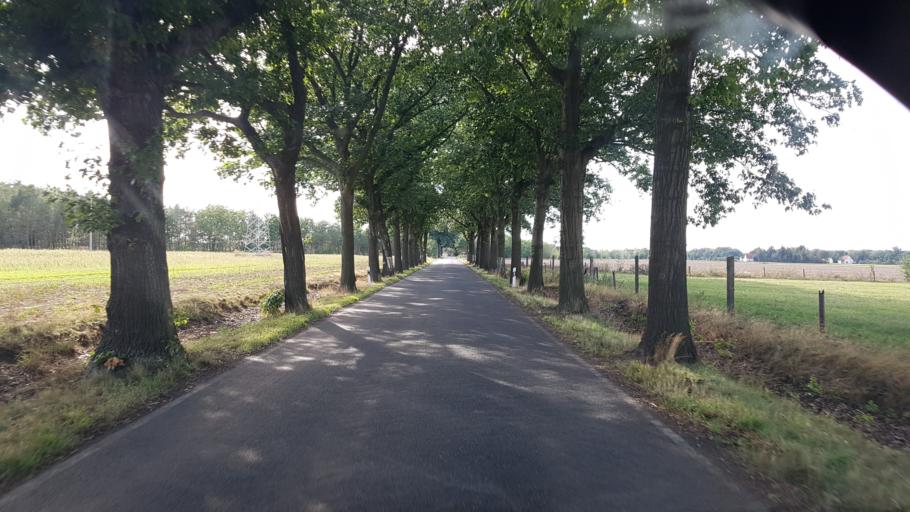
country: DE
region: Brandenburg
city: Welzow
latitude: 51.5566
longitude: 14.1440
